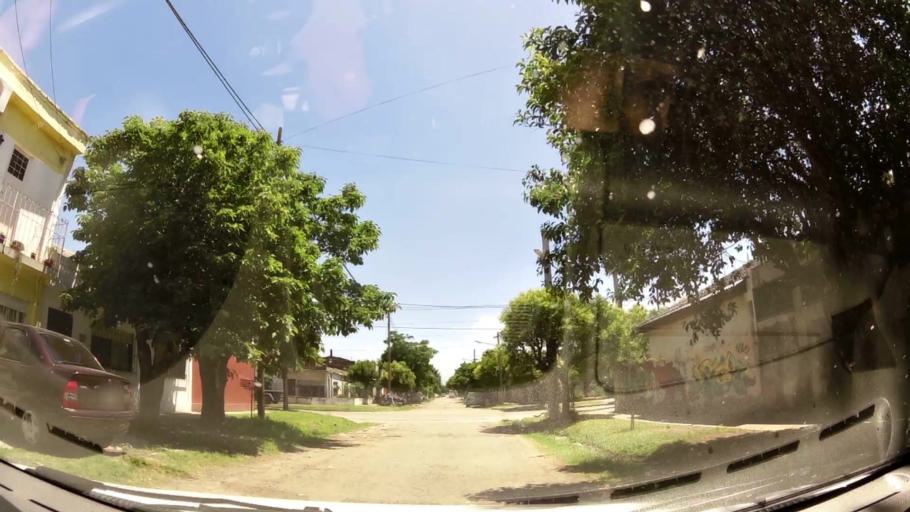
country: AR
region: Buenos Aires
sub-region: Partido de Merlo
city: Merlo
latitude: -34.6465
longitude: -58.7080
